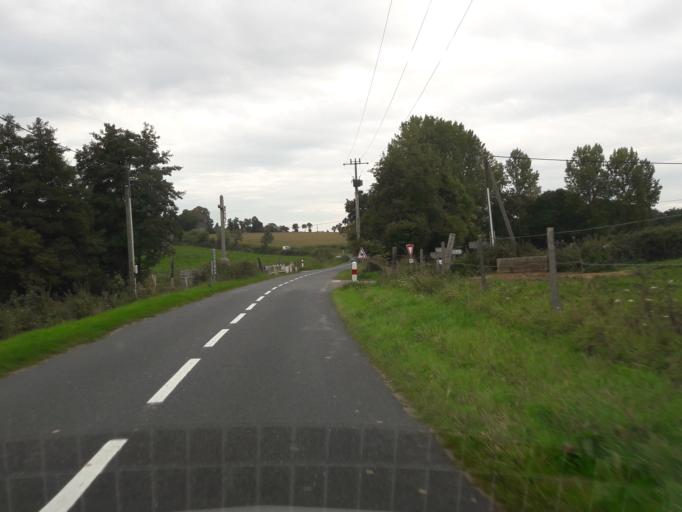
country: FR
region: Lower Normandy
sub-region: Departement du Calvados
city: Bayeux
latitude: 49.1972
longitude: -0.7208
